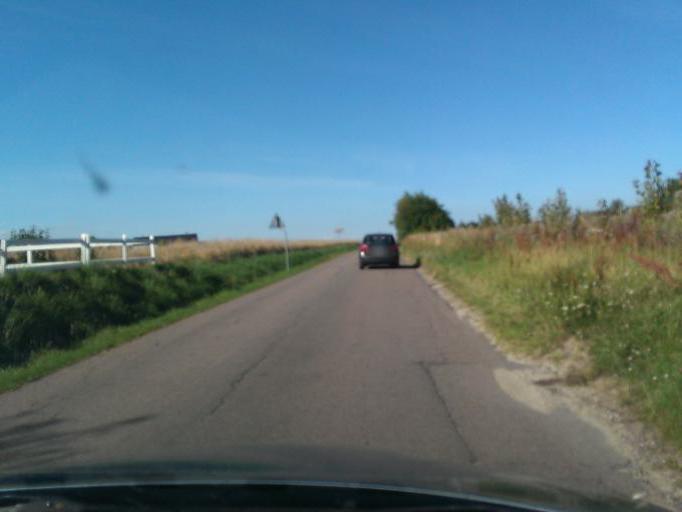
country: DK
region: Central Jutland
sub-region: Odder Kommune
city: Odder
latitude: 55.8894
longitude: 10.1219
